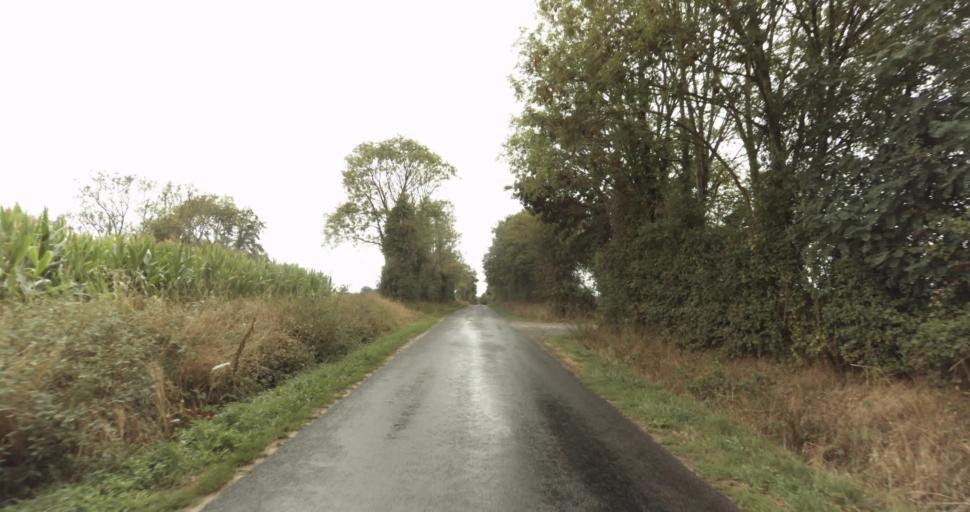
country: FR
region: Lower Normandy
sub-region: Departement de l'Orne
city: Sainte-Gauburge-Sainte-Colombe
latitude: 48.7452
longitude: 0.4485
